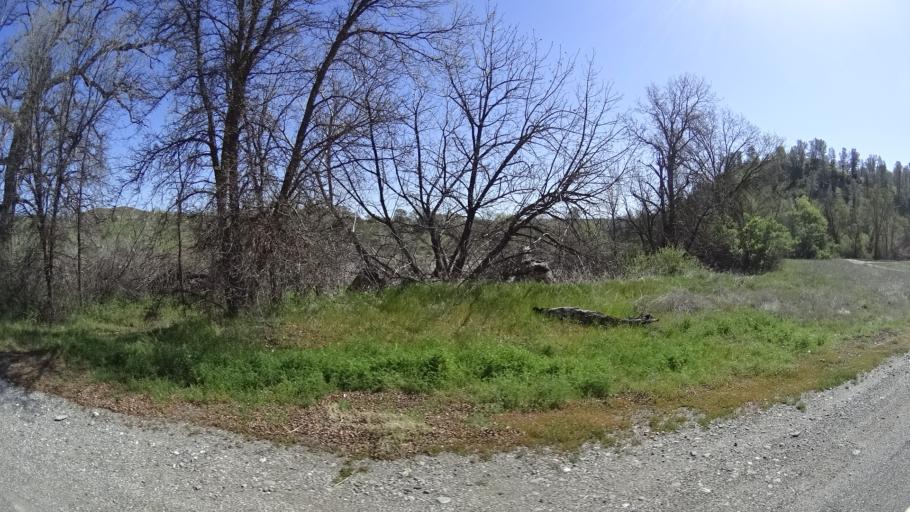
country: US
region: California
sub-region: Glenn County
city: Orland
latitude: 39.6709
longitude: -122.5259
